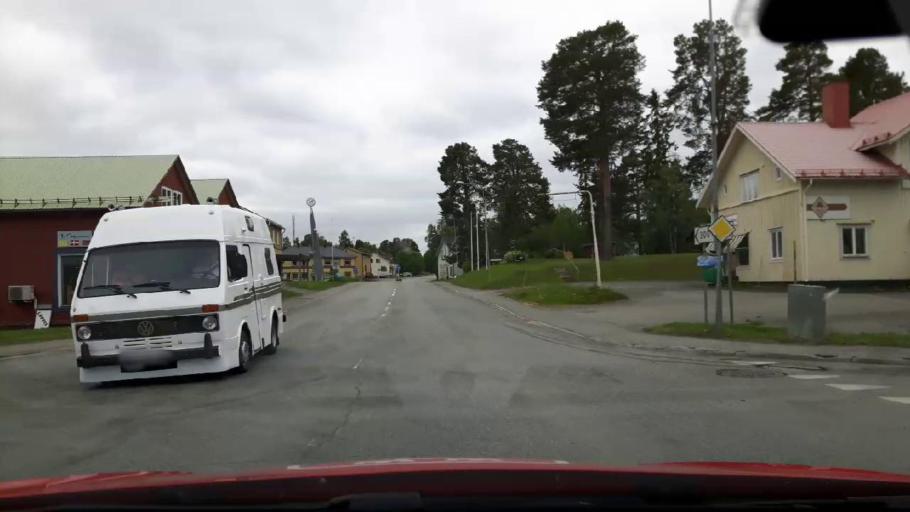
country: SE
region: Jaemtland
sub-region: Stroemsunds Kommun
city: Stroemsund
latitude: 63.5819
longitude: 15.3522
